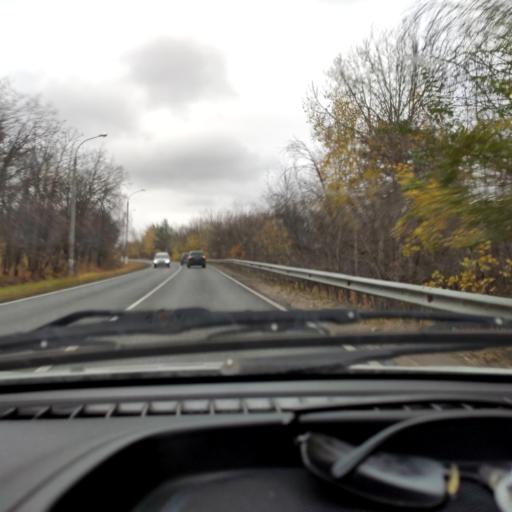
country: RU
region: Samara
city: Tol'yatti
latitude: 53.4734
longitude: 49.4035
